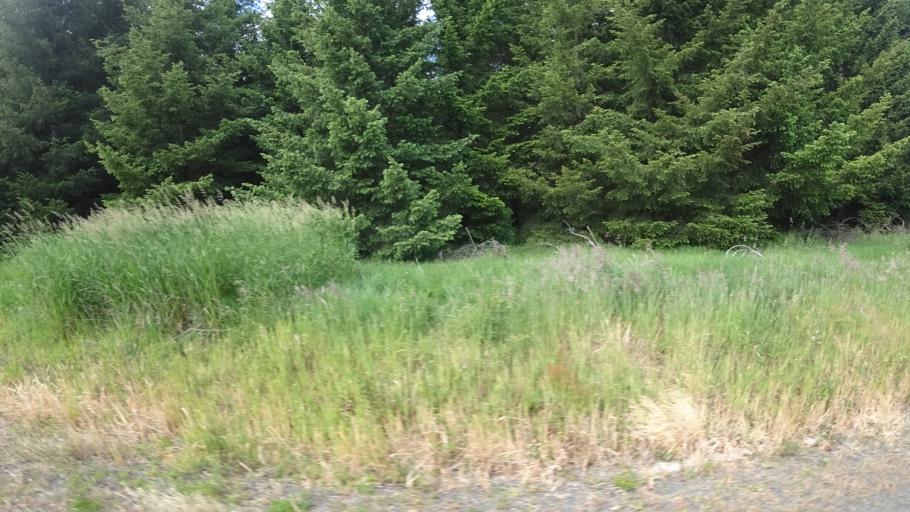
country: US
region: Oregon
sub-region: Washington County
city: Bethany
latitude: 45.6064
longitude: -122.8378
